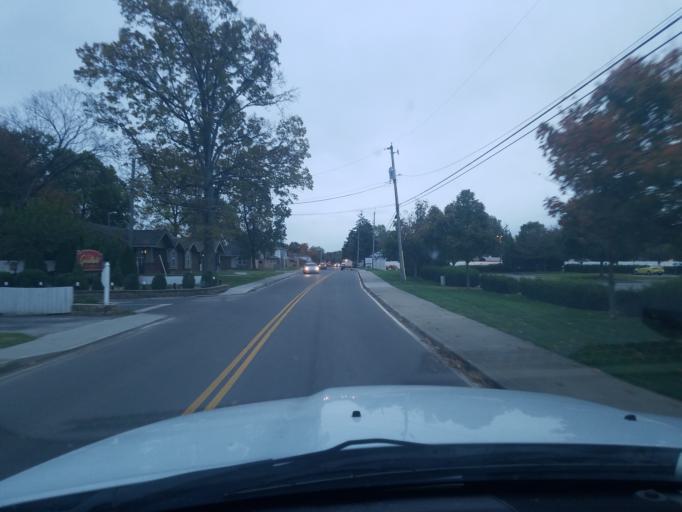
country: US
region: Indiana
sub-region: Floyd County
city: New Albany
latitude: 38.3021
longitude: -85.8312
